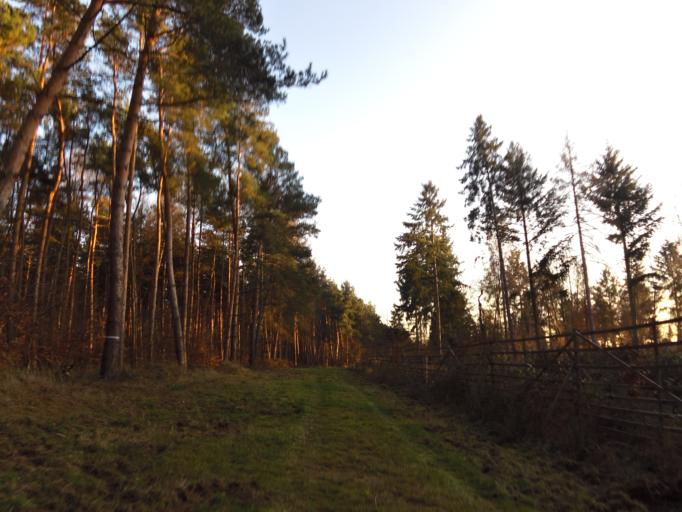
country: DE
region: Hesse
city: Morfelden-Walldorf
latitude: 49.9979
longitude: 8.6162
